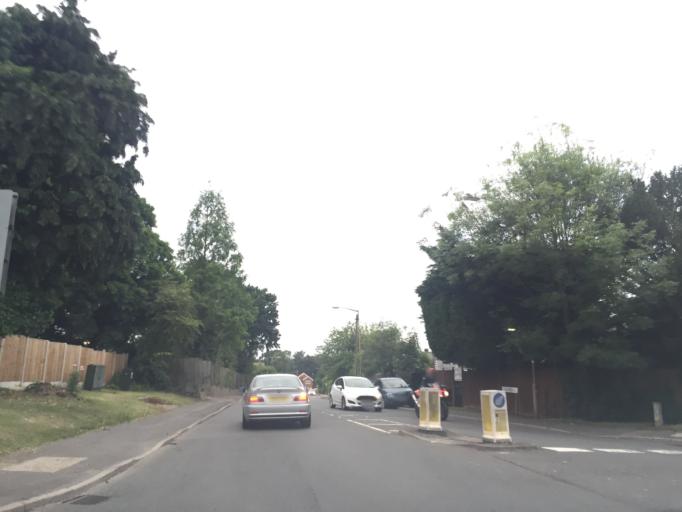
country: GB
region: England
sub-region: Essex
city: Chipping Ongar
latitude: 51.6971
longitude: 0.2436
